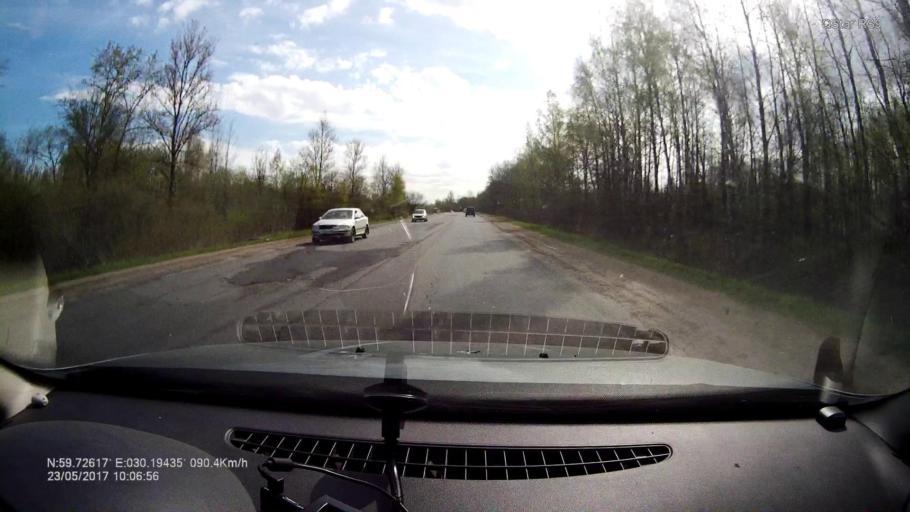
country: RU
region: St.-Petersburg
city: Gorelovo
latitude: 59.7261
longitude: 30.1953
